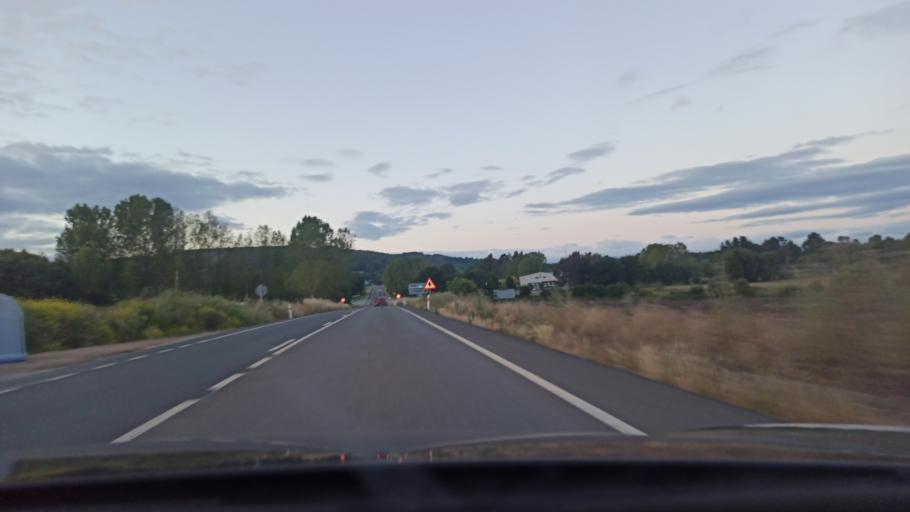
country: ES
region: Galicia
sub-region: Provincia de Lugo
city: Guntin
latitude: 42.9127
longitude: -7.6659
